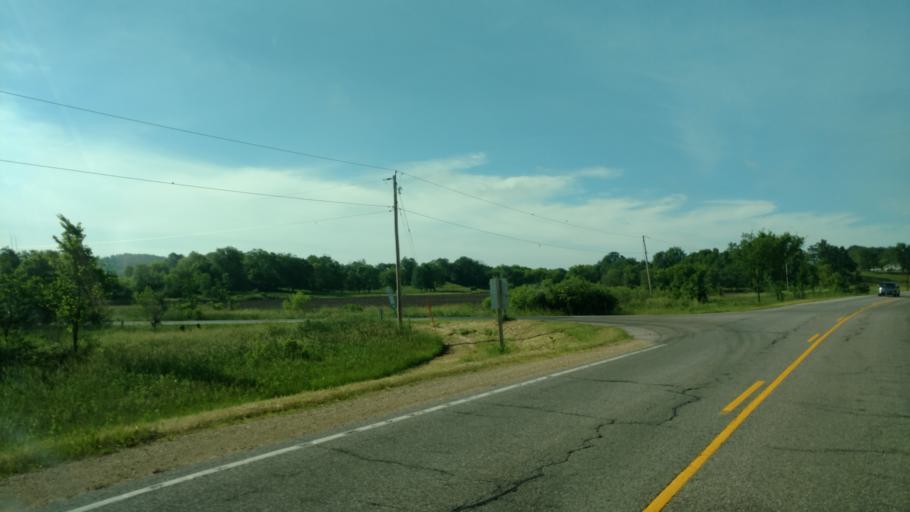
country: US
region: Wisconsin
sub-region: Sauk County
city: Reedsburg
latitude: 43.5626
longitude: -90.1330
